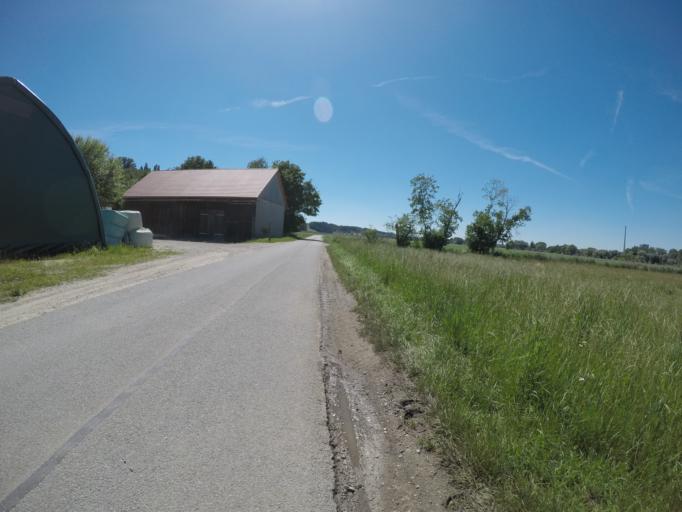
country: DE
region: Bavaria
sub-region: Upper Bavaria
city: Haag an der Amper
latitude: 48.4443
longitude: 11.8269
